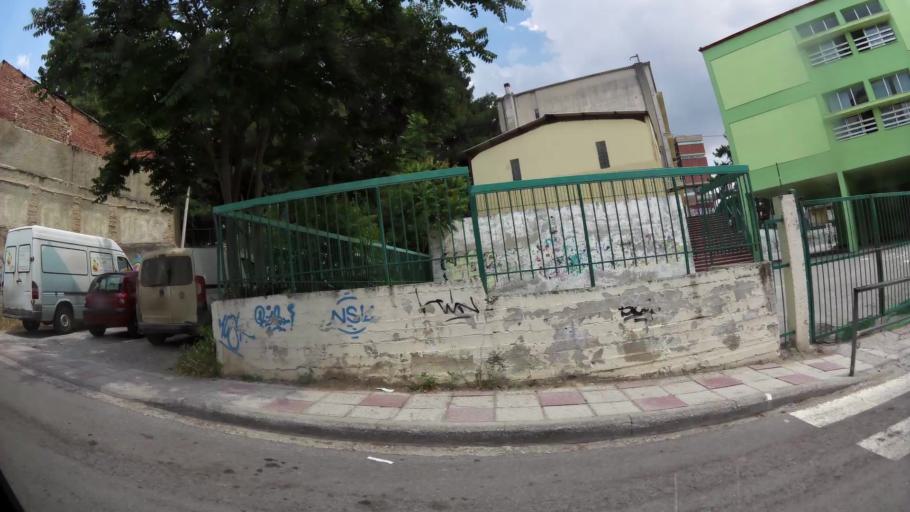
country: GR
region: West Macedonia
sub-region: Nomos Kozanis
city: Kozani
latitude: 40.3031
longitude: 21.7920
